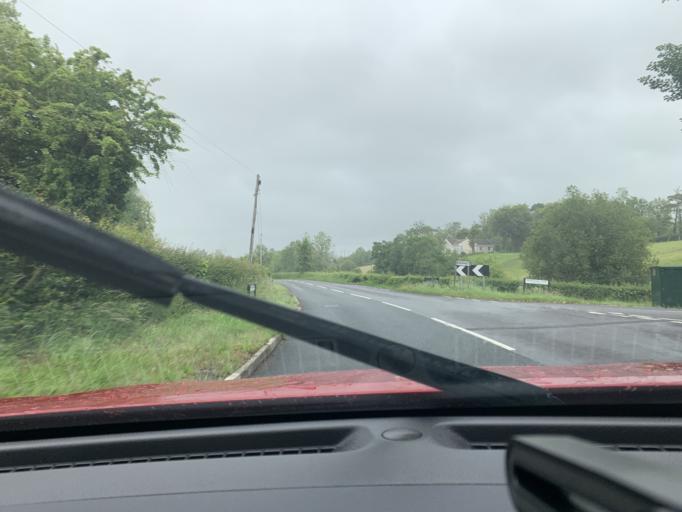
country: GB
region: Northern Ireland
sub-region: Fermanagh District
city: Enniskillen
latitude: 54.3056
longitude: -7.6865
